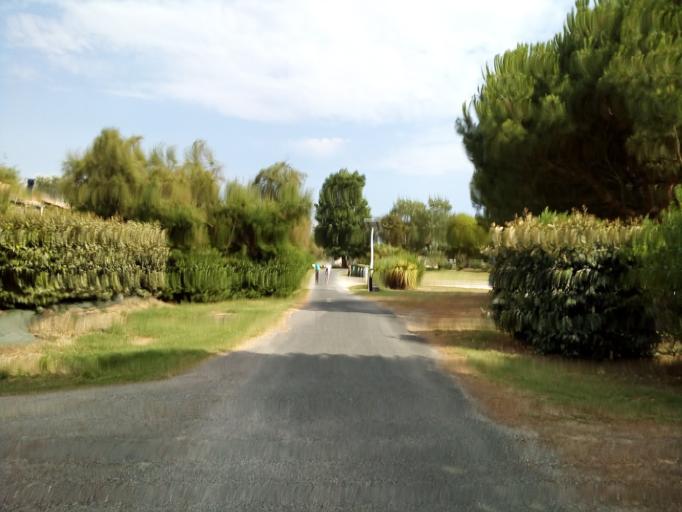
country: FR
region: Poitou-Charentes
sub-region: Departement de la Charente-Maritime
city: Boyard-Ville
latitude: 45.9498
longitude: -1.2479
